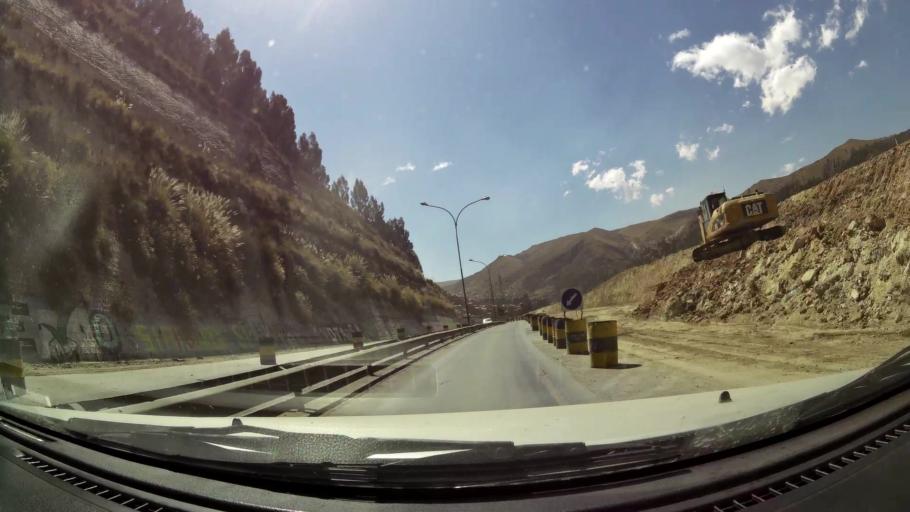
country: BO
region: La Paz
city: La Paz
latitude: -16.4664
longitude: -68.1553
